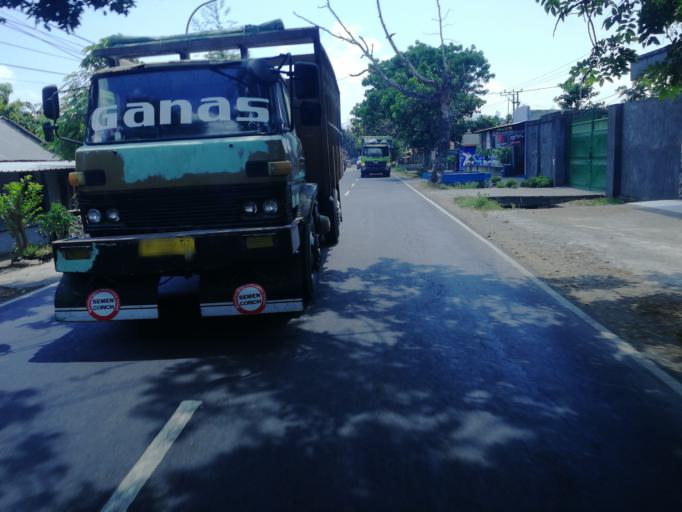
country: ID
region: West Nusa Tenggara
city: Jelateng Timur
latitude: -8.7037
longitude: 116.0918
